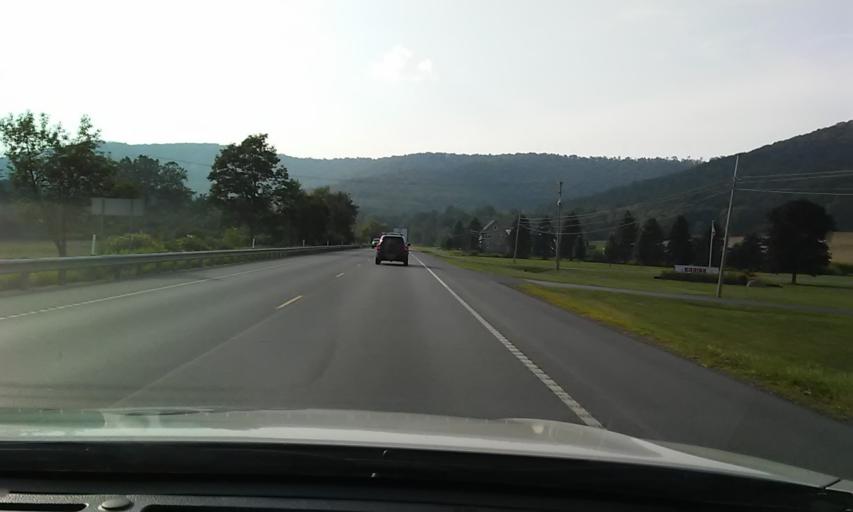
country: US
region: Pennsylvania
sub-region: McKean County
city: Port Allegany
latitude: 41.7895
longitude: -78.2076
